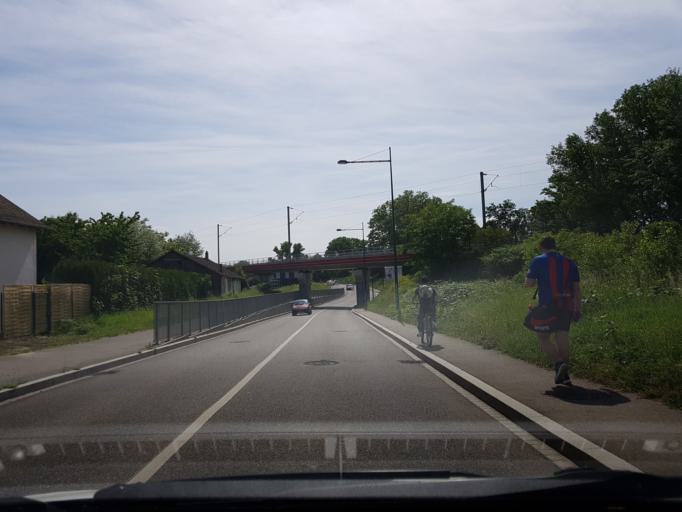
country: FR
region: Alsace
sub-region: Departement du Haut-Rhin
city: Mulhouse
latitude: 47.7361
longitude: 7.3288
